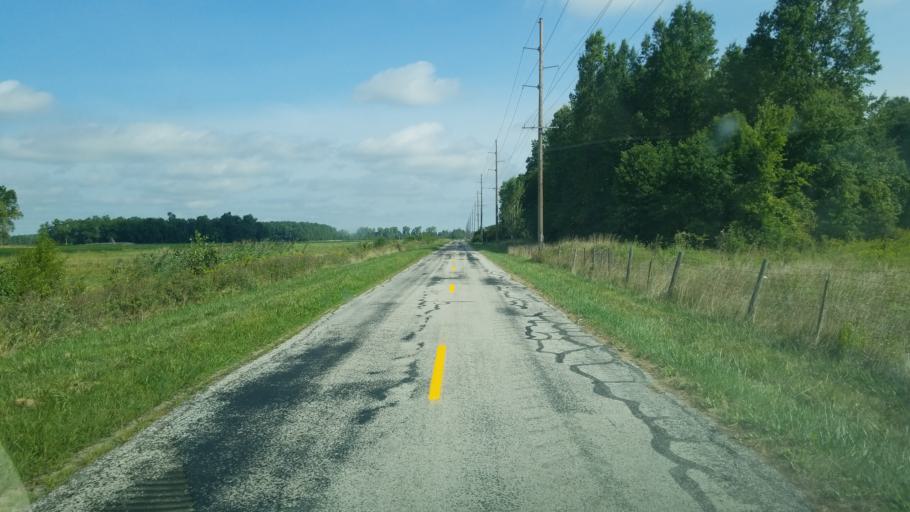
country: US
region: Ohio
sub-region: Wyandot County
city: Upper Sandusky
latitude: 40.6775
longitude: -83.3241
